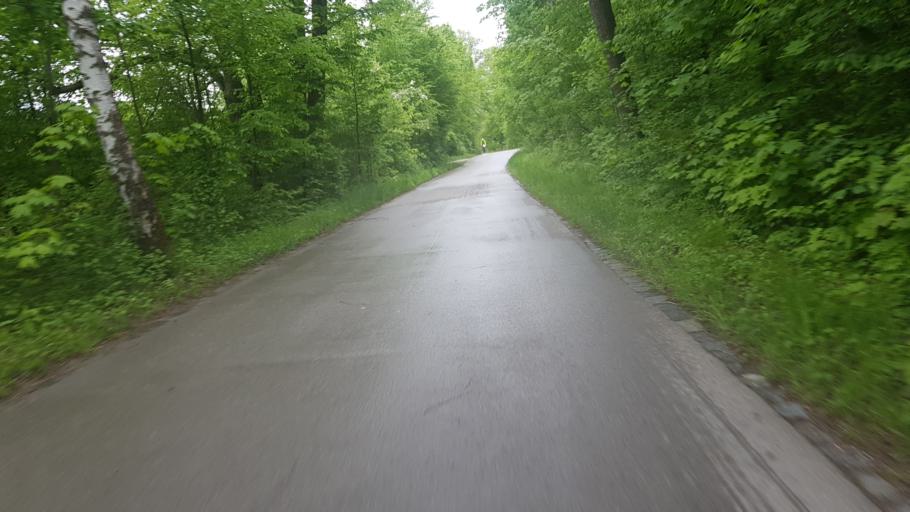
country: DE
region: Bavaria
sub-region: Upper Bavaria
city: Munich
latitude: 48.1142
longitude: 11.5608
